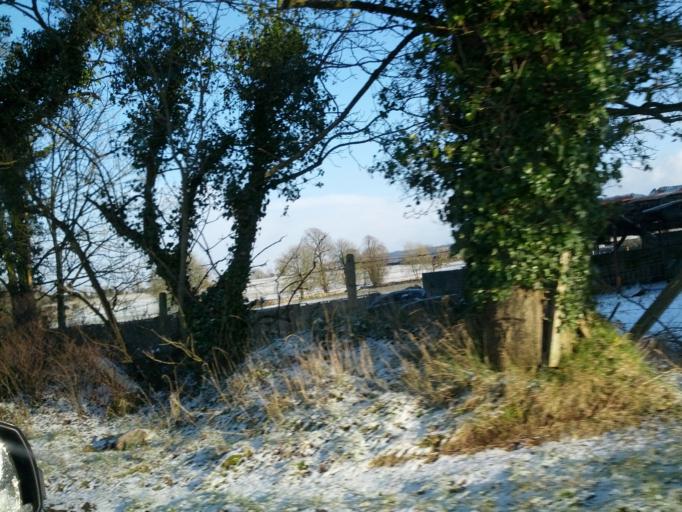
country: IE
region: Connaught
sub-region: County Galway
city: Athenry
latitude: 53.1780
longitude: -8.7358
